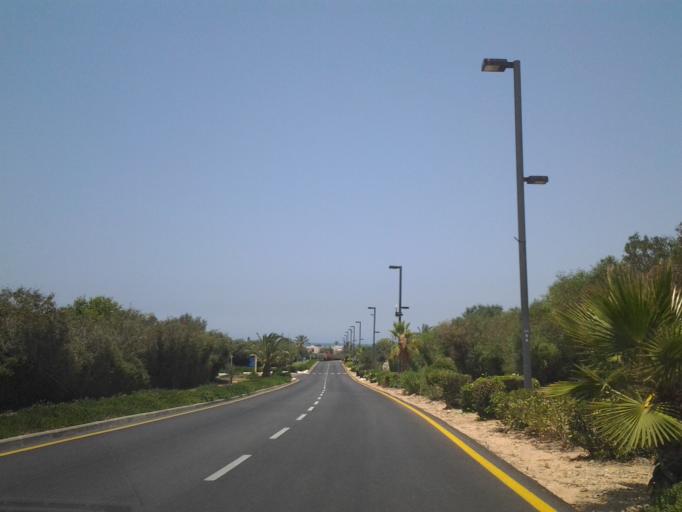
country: IL
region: Haifa
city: Qesarya
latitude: 32.5257
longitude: 34.9087
